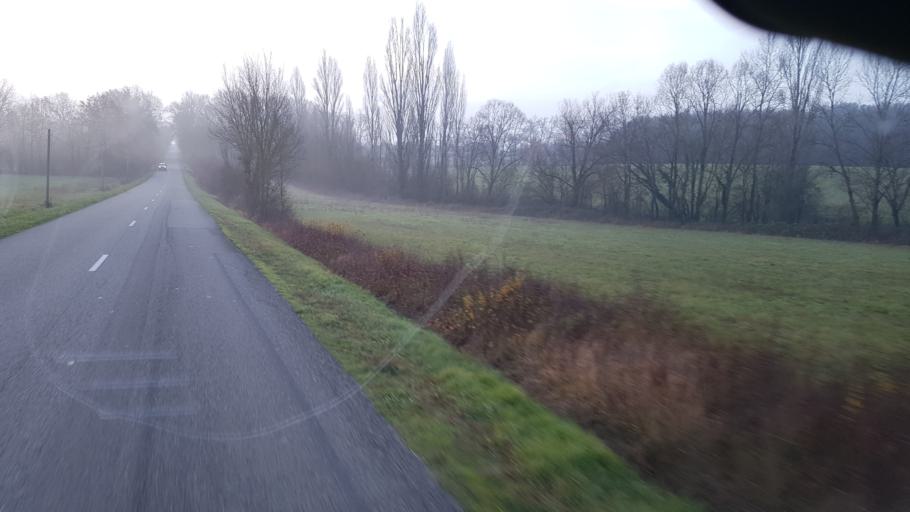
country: FR
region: Midi-Pyrenees
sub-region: Departement du Tarn-et-Garonne
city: Monteils
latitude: 44.1209
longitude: 1.5875
